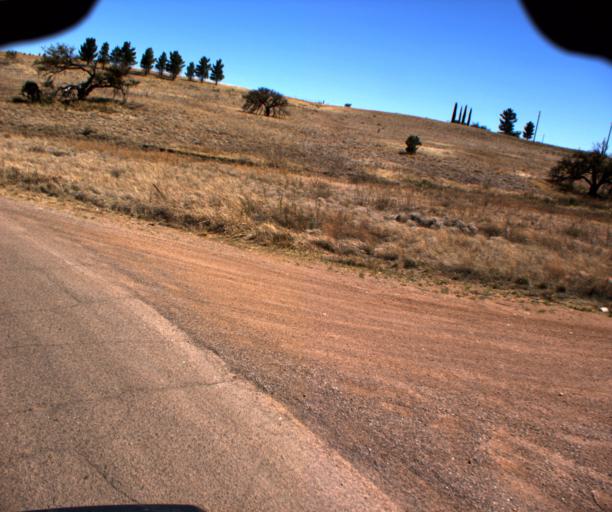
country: US
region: Arizona
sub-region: Cochise County
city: Huachuca City
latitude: 31.6008
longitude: -110.5785
